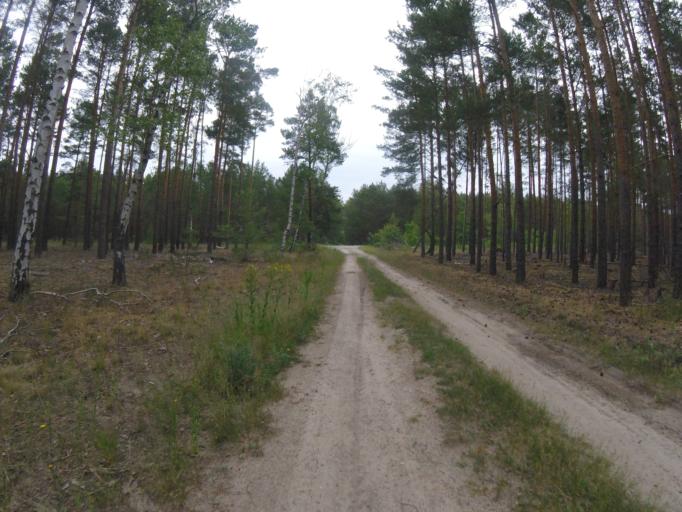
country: DE
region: Brandenburg
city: Gross Koris
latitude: 52.1965
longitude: 13.6637
